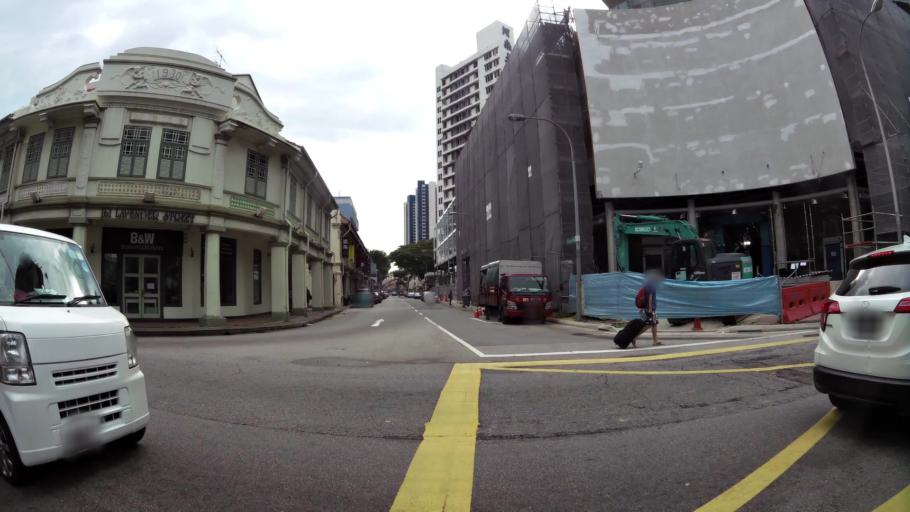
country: SG
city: Singapore
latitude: 1.3132
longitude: 103.8608
